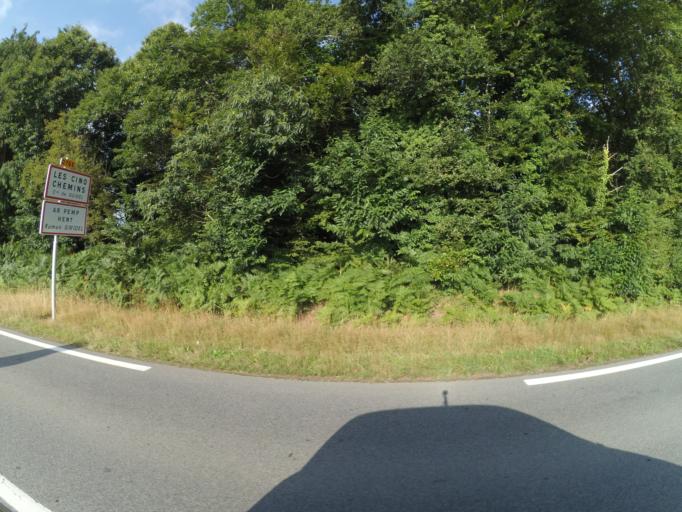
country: FR
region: Brittany
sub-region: Departement du Morbihan
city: Gestel
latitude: 47.8035
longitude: -3.4792
